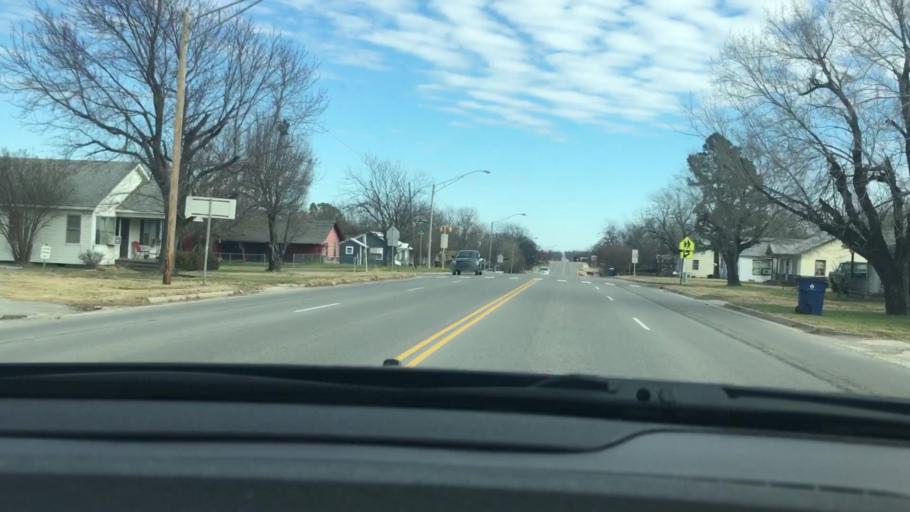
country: US
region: Oklahoma
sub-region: Garvin County
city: Stratford
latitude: 34.7966
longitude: -96.9595
